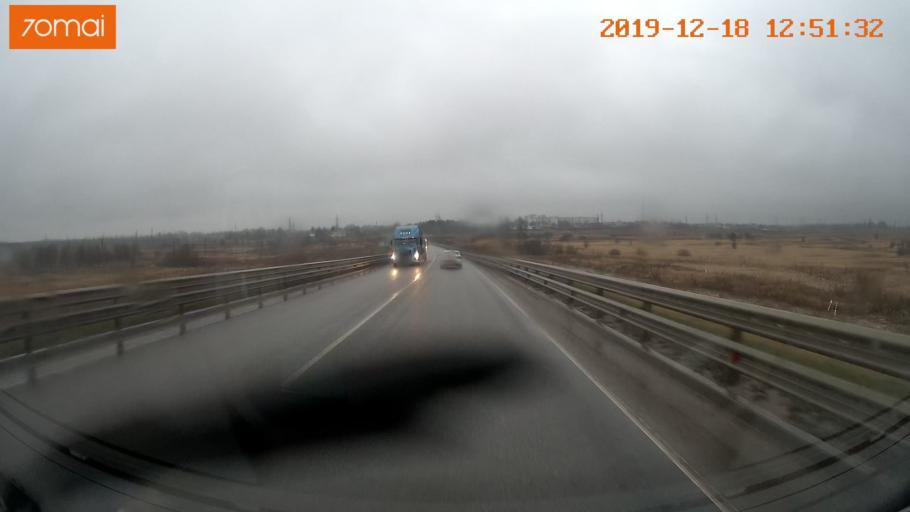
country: RU
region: Moskovskaya
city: Klin
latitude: 56.3039
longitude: 36.6840
